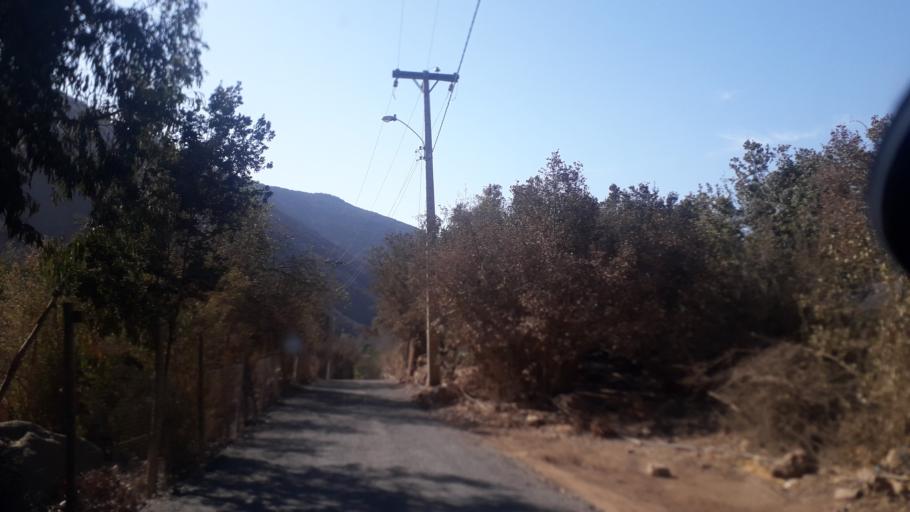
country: CL
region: Valparaiso
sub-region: Provincia de Marga Marga
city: Limache
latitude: -33.0801
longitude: -71.1000
